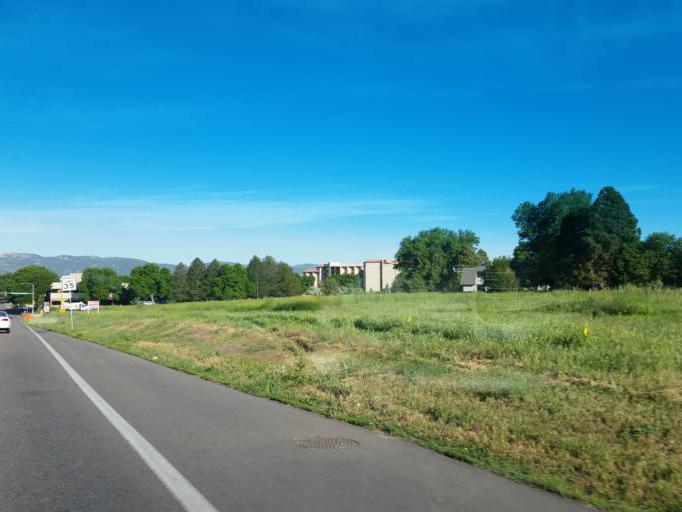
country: US
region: Colorado
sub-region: Larimer County
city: Fort Collins
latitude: 40.5381
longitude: -105.0678
